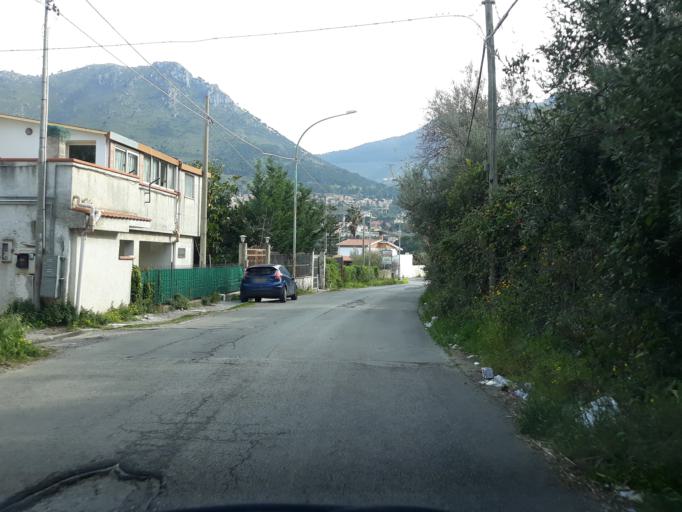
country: IT
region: Sicily
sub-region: Palermo
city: Piano Maglio-Blandino
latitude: 38.0694
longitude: 13.3050
